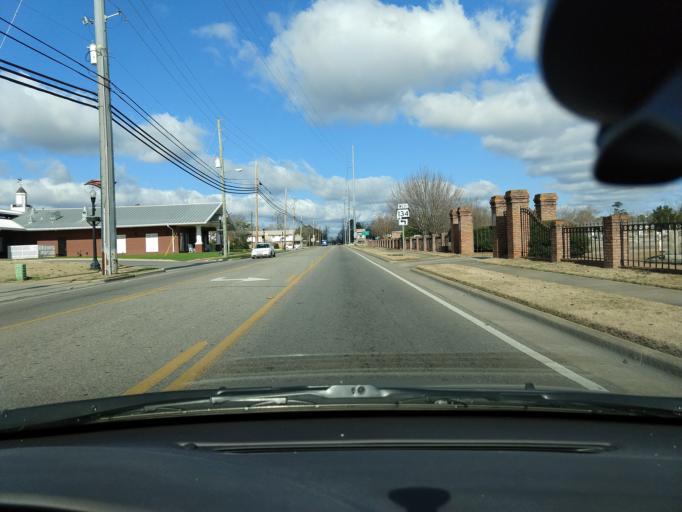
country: US
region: Alabama
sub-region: Coffee County
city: Enterprise
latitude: 31.3195
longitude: -85.8581
